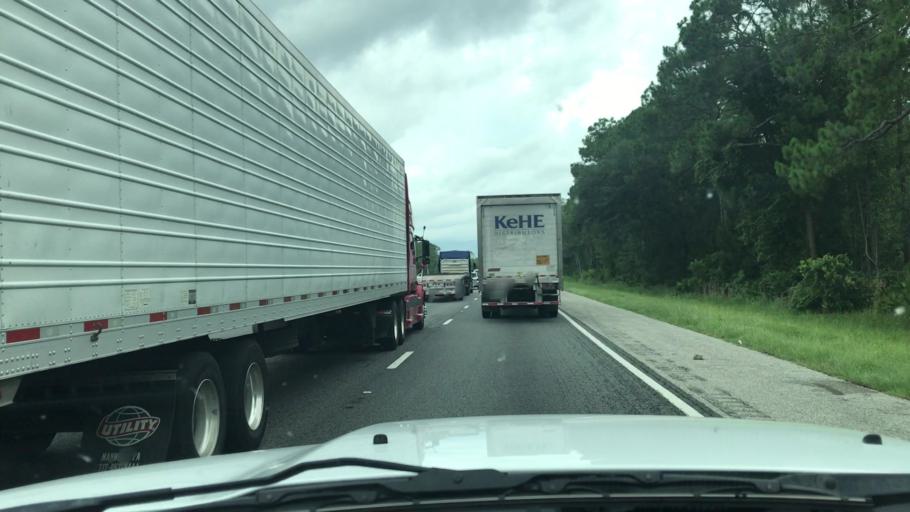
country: US
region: Florida
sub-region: Saint Johns County
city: Butler Beach
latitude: 29.6758
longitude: -81.3100
